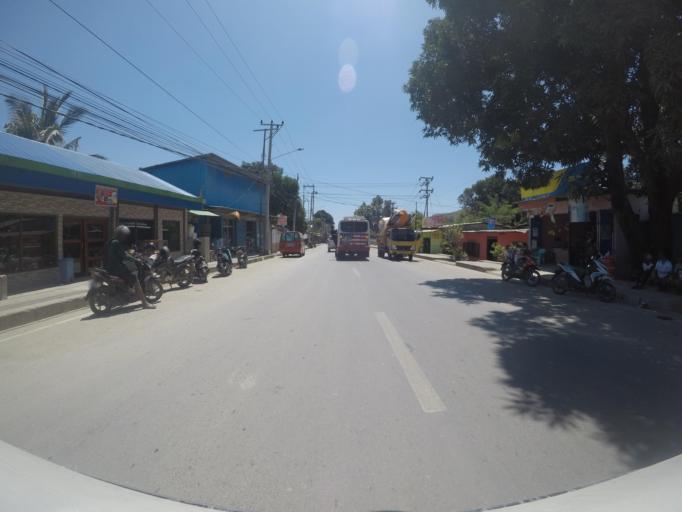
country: TL
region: Dili
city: Dili
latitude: -8.5651
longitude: 125.6120
